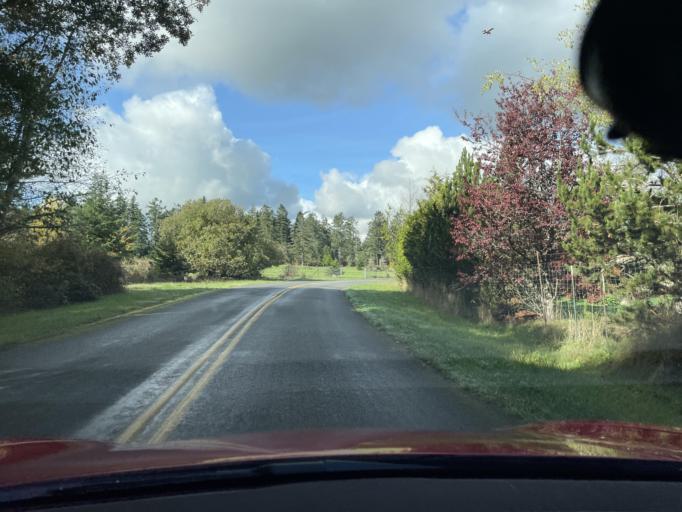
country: US
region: Washington
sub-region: San Juan County
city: Friday Harbor
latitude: 48.5058
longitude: -123.0197
